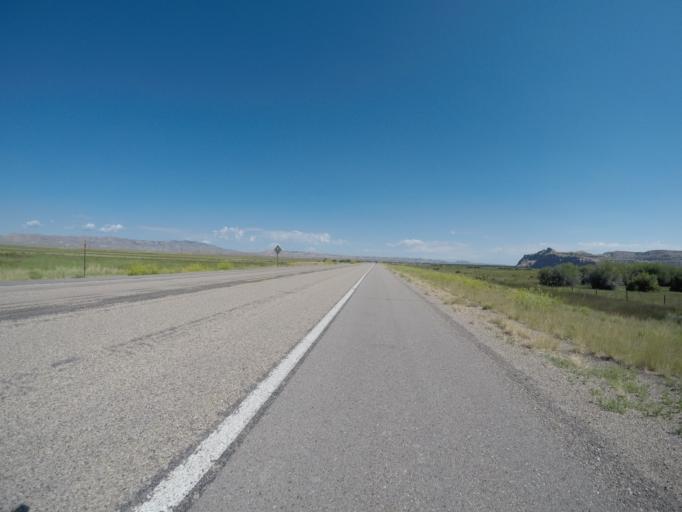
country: US
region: Wyoming
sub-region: Sublette County
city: Marbleton
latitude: 42.2290
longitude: -110.1924
